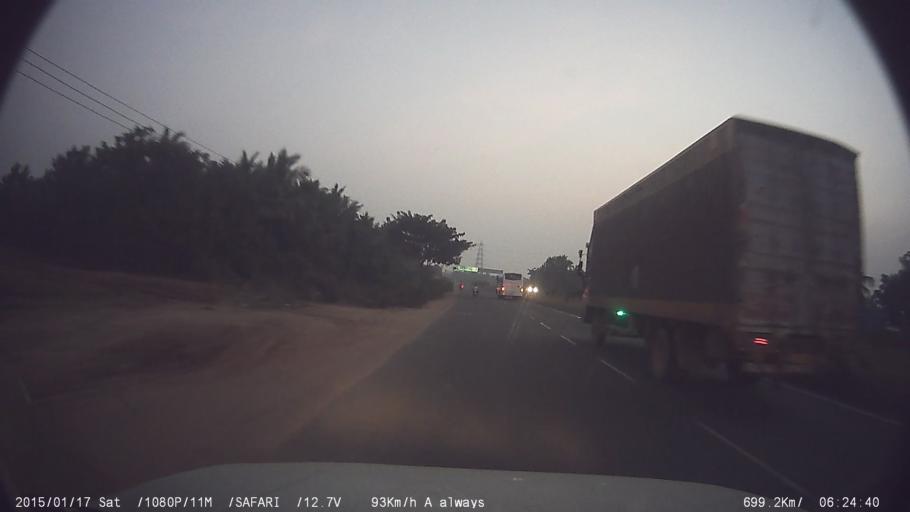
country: IN
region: Tamil Nadu
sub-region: Kancheepuram
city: Sriperumbudur
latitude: 12.9186
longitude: 79.8662
